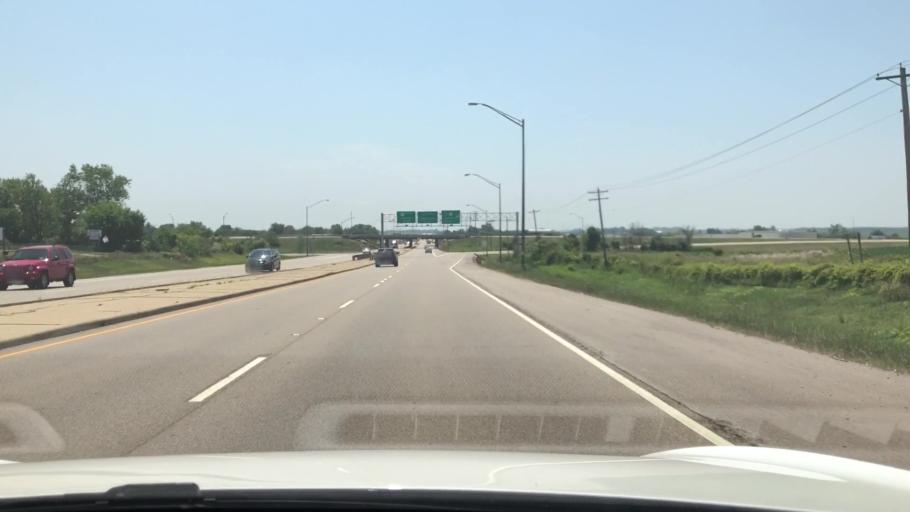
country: US
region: Illinois
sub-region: McLean County
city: Bloomington
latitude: 40.4399
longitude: -88.9909
